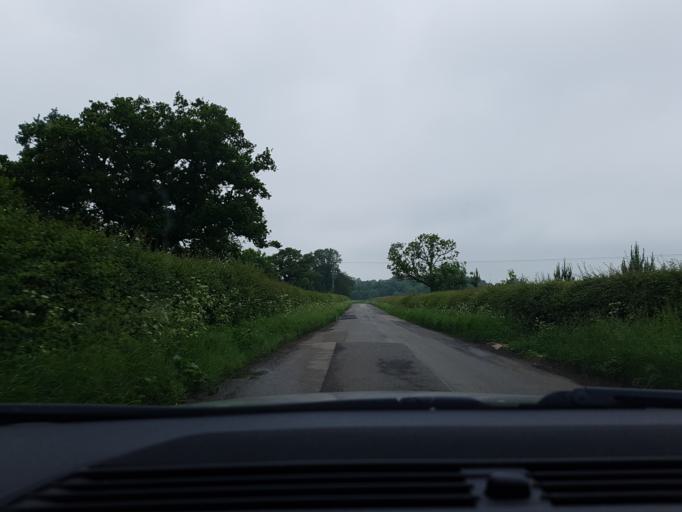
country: GB
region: England
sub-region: Buckinghamshire
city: Steeple Claydon
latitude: 51.9287
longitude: -0.9636
